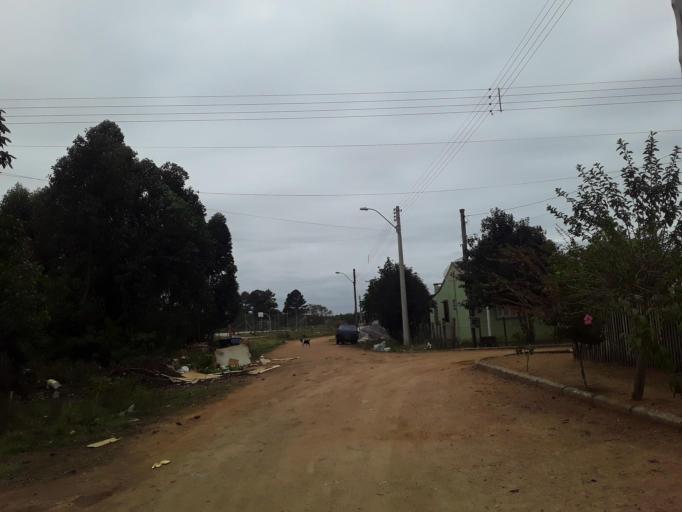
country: BR
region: Rio Grande do Sul
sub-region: Sao Lourenco Do Sul
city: Sao Lourenco do Sul
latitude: -31.3396
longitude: -51.9896
